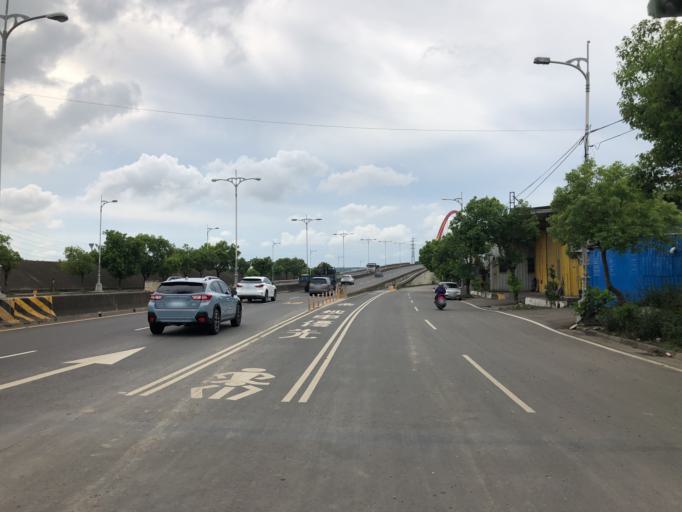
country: TW
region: Taiwan
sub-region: Changhua
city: Chang-hua
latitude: 24.0960
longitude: 120.6286
